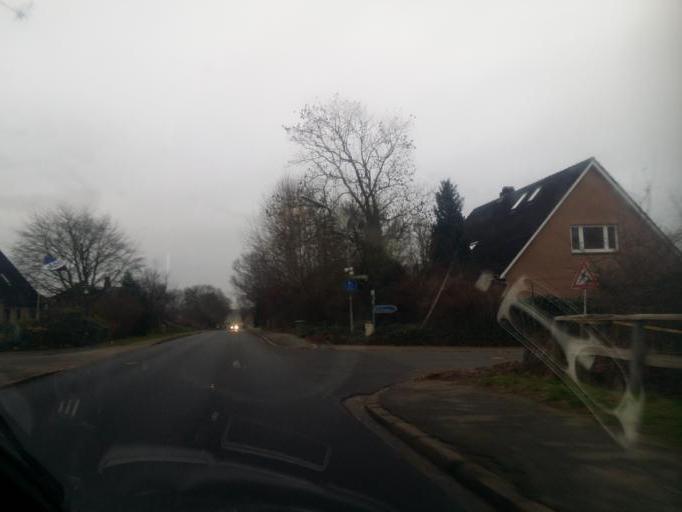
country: DE
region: Schleswig-Holstein
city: Suderheistedt
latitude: 54.2325
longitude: 9.1443
